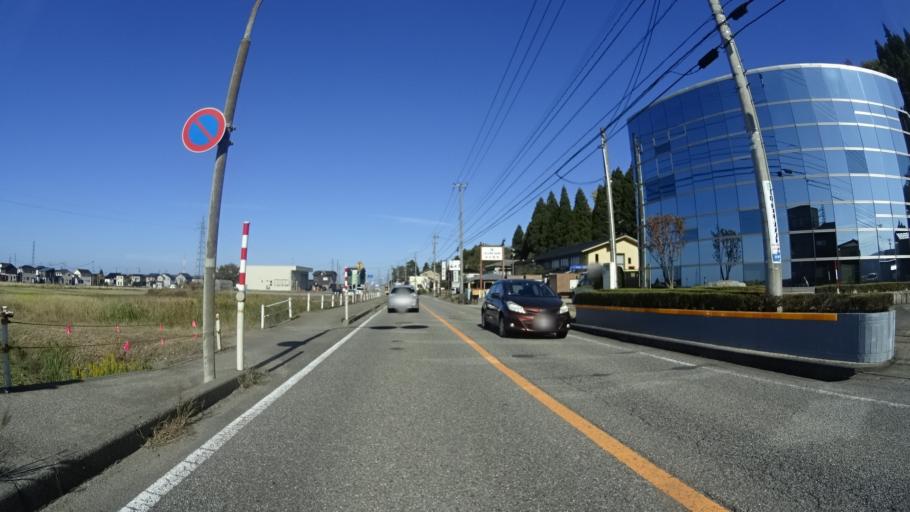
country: JP
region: Ishikawa
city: Tsurugi-asahimachi
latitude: 36.4699
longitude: 136.6175
